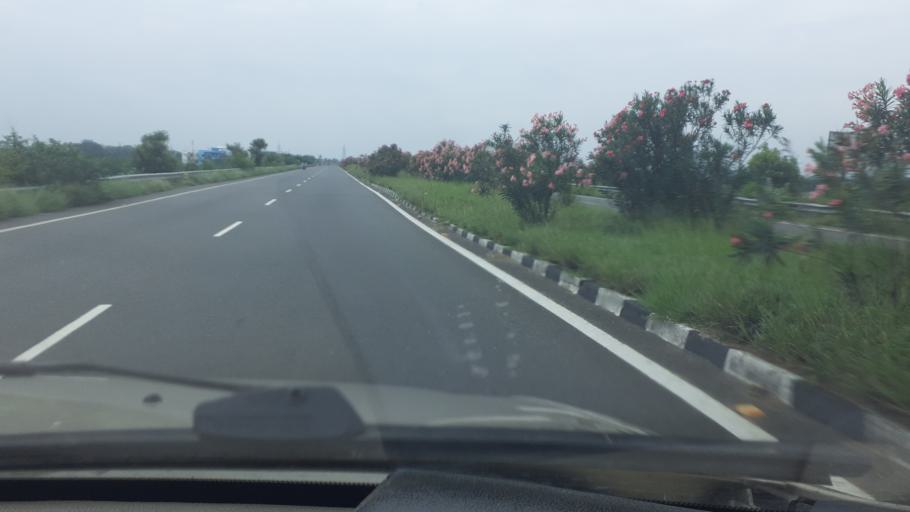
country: IN
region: Tamil Nadu
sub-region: Madurai
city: Tirupparangunram
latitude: 9.8357
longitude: 77.9961
